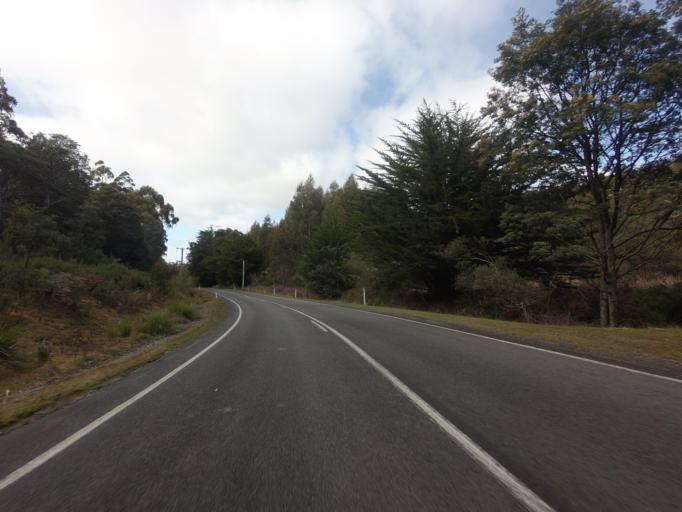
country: AU
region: Tasmania
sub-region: Huon Valley
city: Geeveston
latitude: -43.4007
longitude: 146.9553
